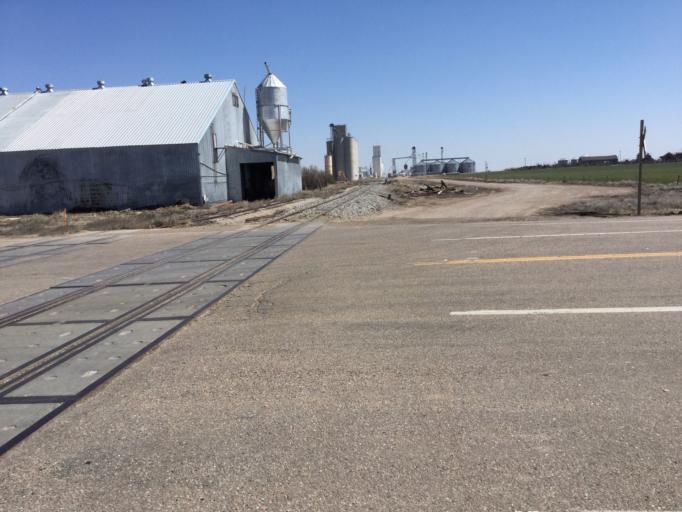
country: US
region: Kansas
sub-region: Stanton County
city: Johnson
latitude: 37.5620
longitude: -101.7620
